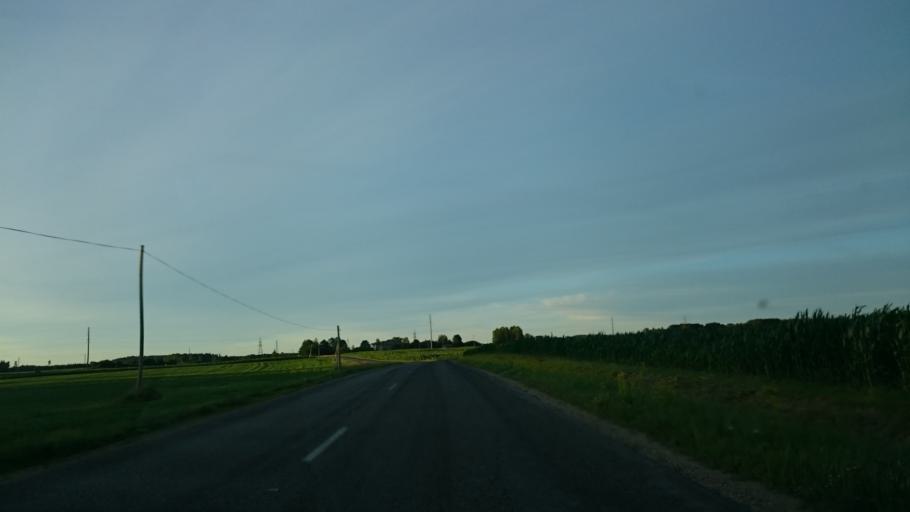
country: LV
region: Saldus Rajons
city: Saldus
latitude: 56.6822
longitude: 22.5014
